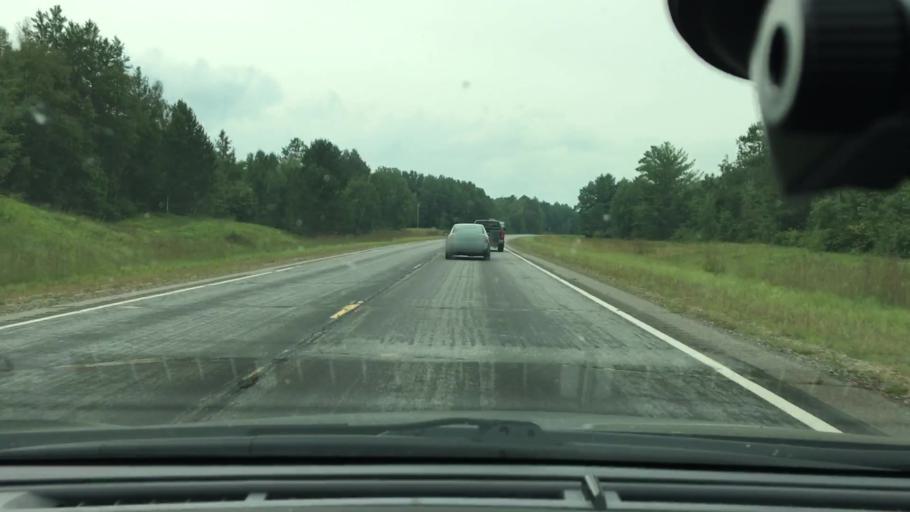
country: US
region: Minnesota
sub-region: Crow Wing County
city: Cross Lake
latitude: 46.6722
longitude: -93.9519
